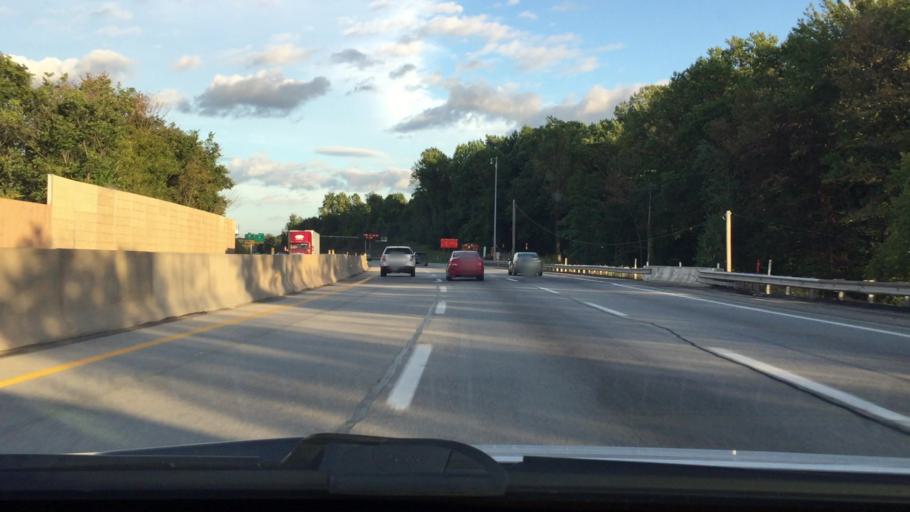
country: US
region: Pennsylvania
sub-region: Bucks County
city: Trevose
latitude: 40.1360
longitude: -74.9907
